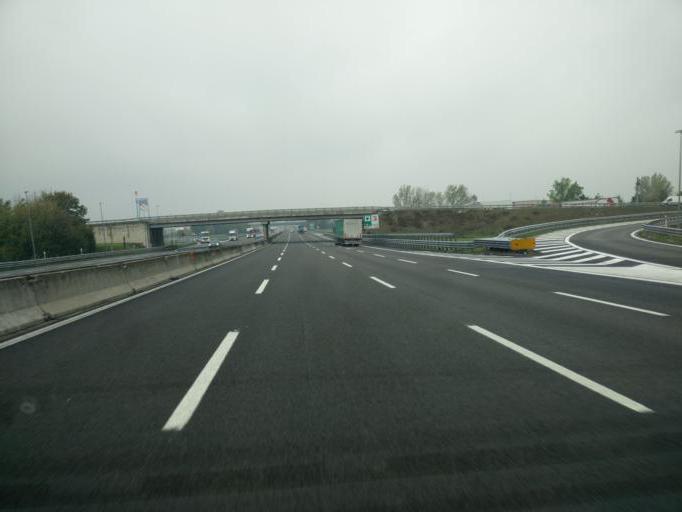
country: IT
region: Emilia-Romagna
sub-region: Provincia di Modena
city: Campogalliano
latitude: 44.6527
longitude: 10.8638
